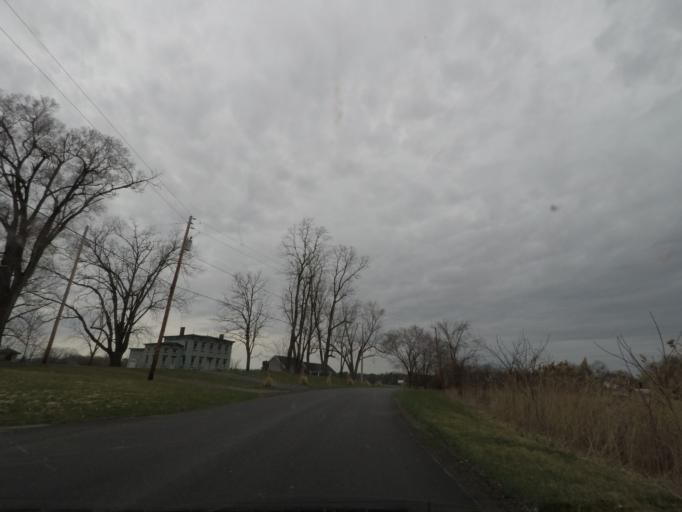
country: US
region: New York
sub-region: Rensselaer County
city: Castleton-on-Hudson
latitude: 42.5590
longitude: -73.7927
